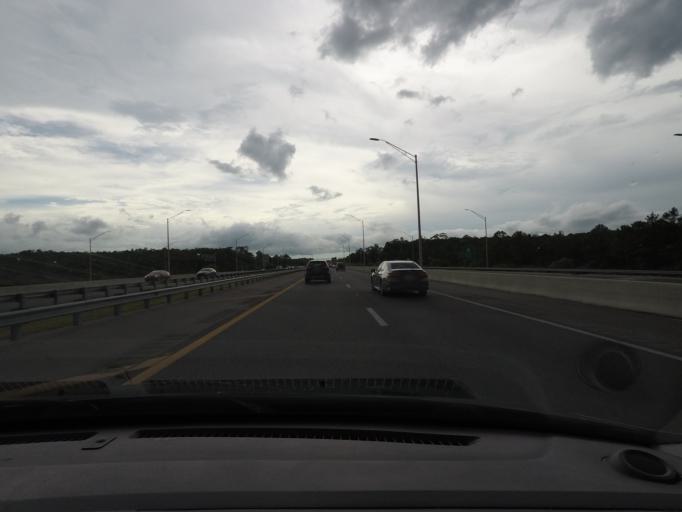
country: US
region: Florida
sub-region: Orange County
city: Alafaya
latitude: 28.4517
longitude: -81.2107
